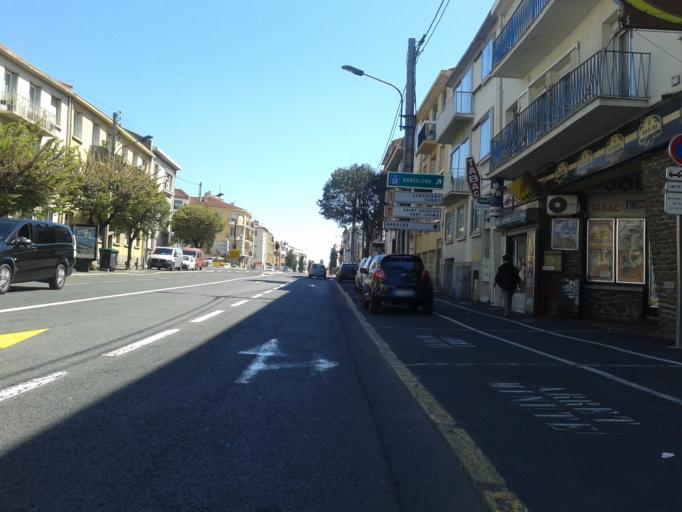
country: FR
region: Languedoc-Roussillon
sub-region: Departement des Pyrenees-Orientales
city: Perpignan
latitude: 42.6913
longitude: 2.8972
